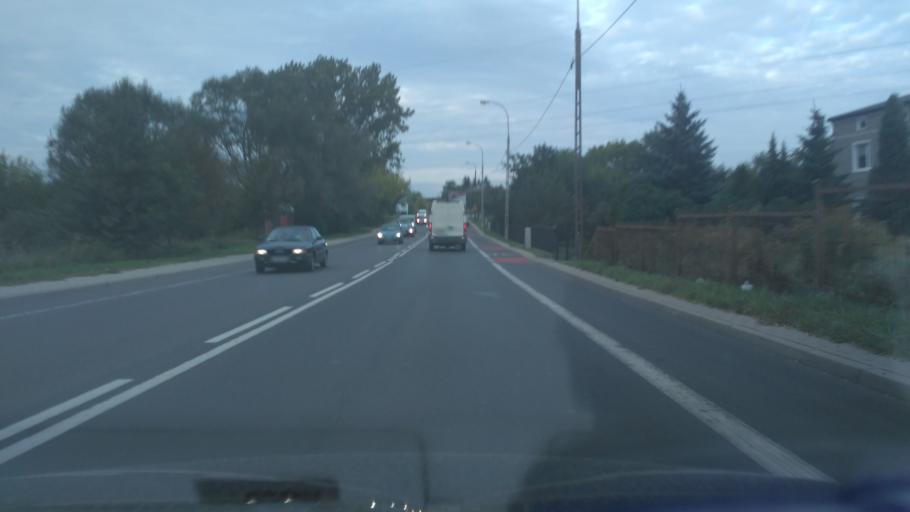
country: PL
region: Lublin Voivodeship
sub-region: Powiat lubelski
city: Jakubowice Murowane
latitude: 51.2583
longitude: 22.6126
